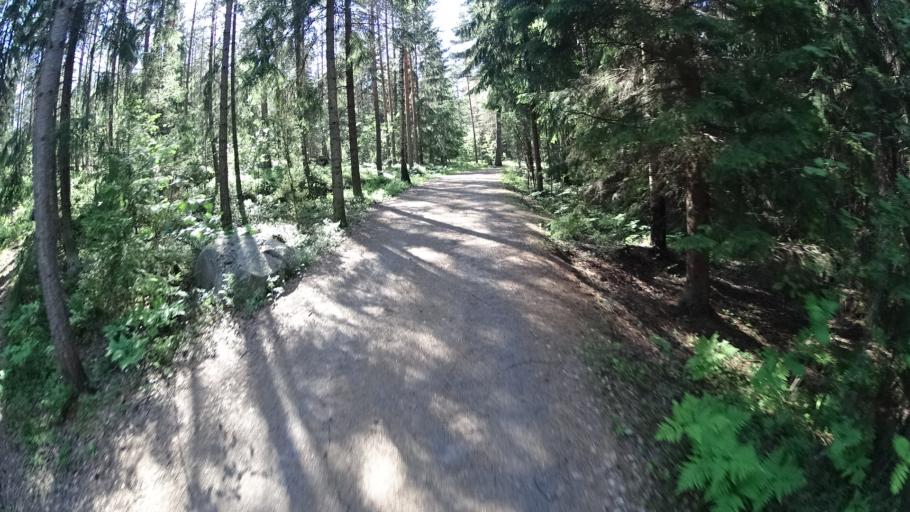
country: FI
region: Uusimaa
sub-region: Helsinki
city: Vantaa
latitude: 60.2350
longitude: 25.1798
